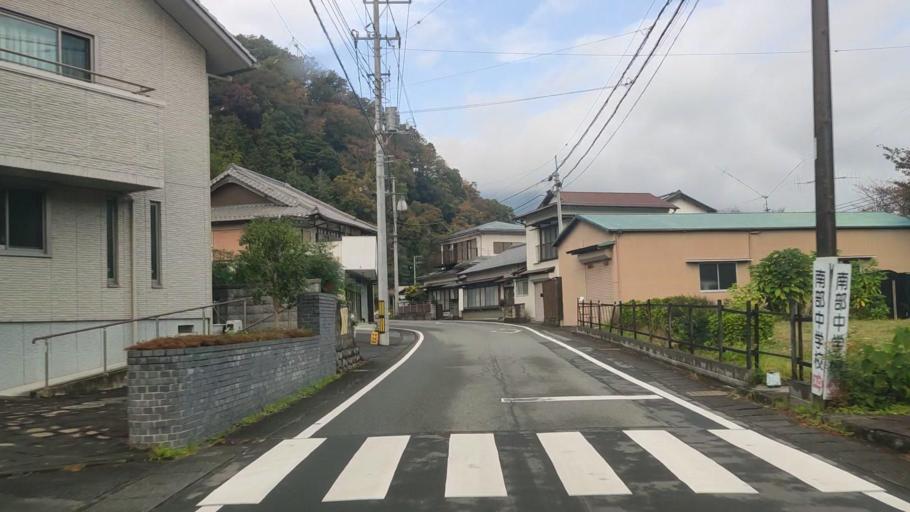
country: JP
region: Shizuoka
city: Fujinomiya
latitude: 35.2908
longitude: 138.4543
